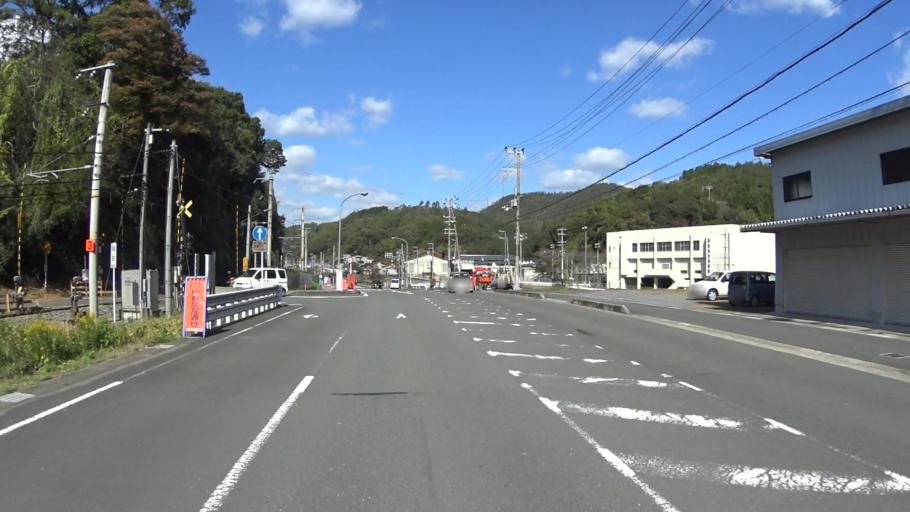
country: JP
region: Kyoto
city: Kameoka
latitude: 35.1576
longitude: 135.5065
